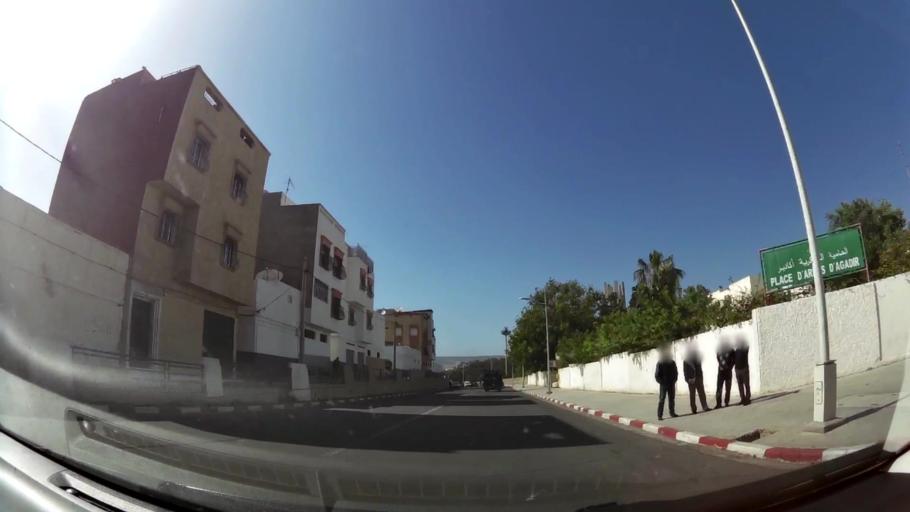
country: MA
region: Souss-Massa-Draa
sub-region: Agadir-Ida-ou-Tnan
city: Agadir
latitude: 30.4162
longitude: -9.5919
